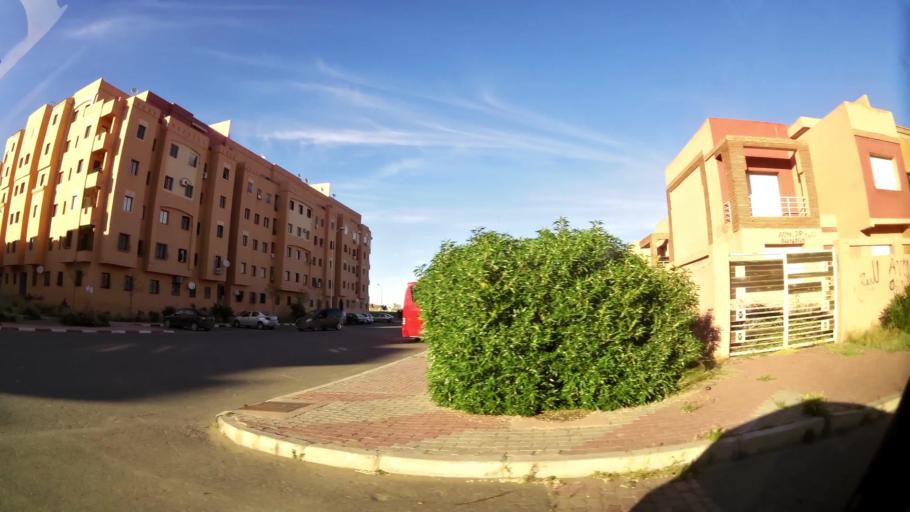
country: MA
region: Marrakech-Tensift-Al Haouz
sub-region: Marrakech
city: Marrakesh
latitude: 31.7629
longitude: -8.1094
